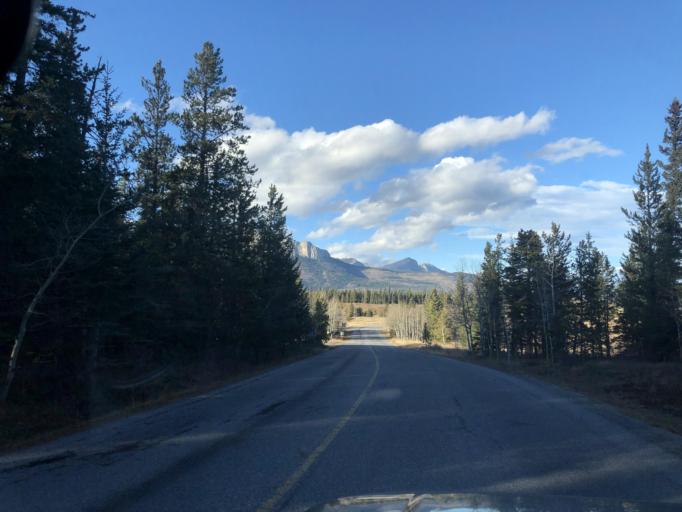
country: CA
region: Alberta
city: Canmore
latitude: 51.0811
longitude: -115.0633
